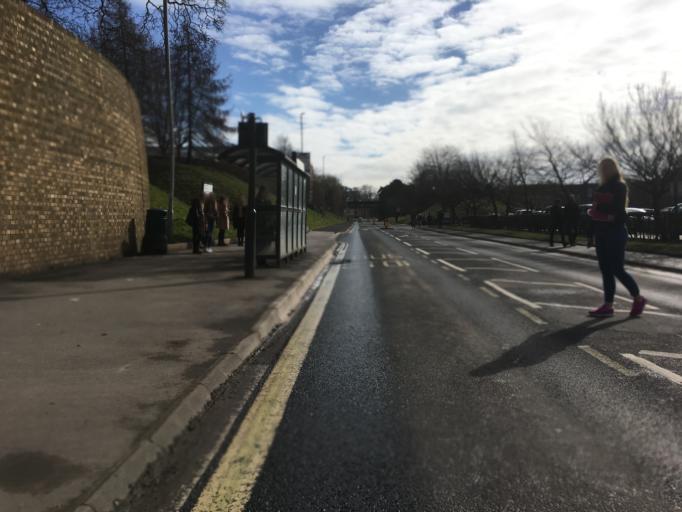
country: GB
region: England
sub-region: City of York
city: Heslington
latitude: 53.9490
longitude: -1.0525
